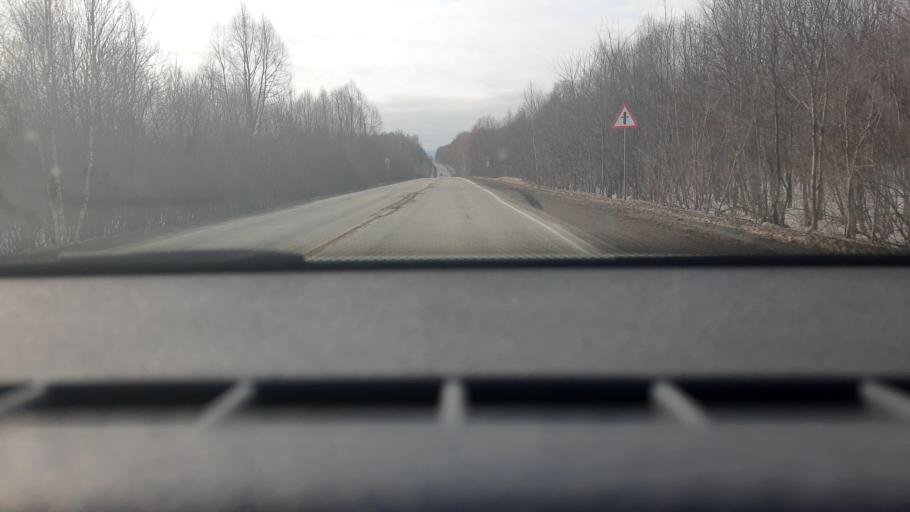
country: RU
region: Chelyabinsk
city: Asha
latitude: 54.9202
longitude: 57.2910
